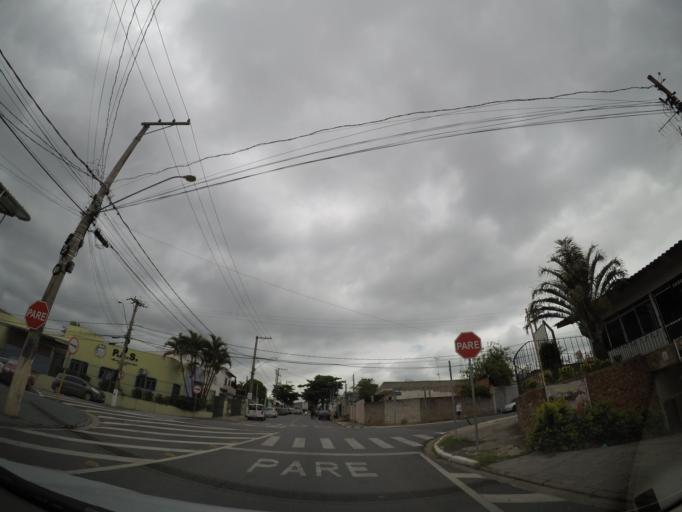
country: BR
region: Sao Paulo
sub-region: Louveira
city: Louveira
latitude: -23.0867
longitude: -46.9769
